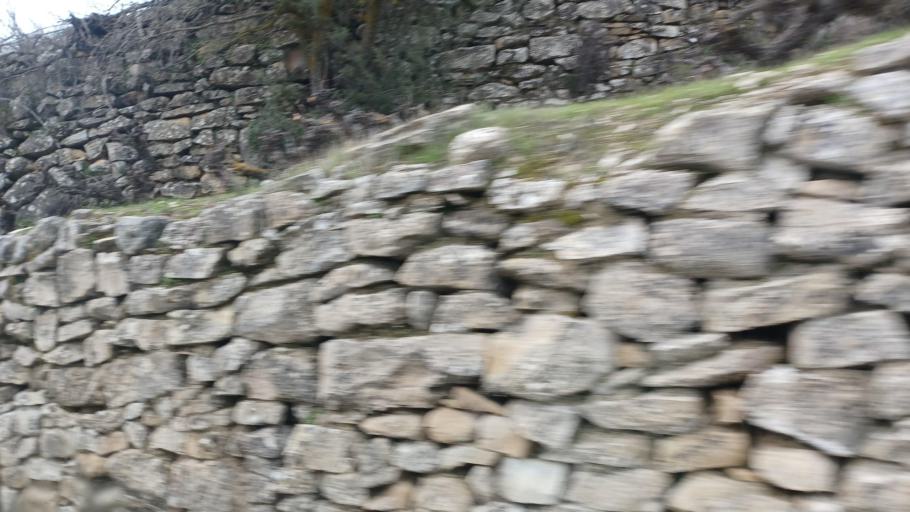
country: CY
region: Limassol
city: Pachna
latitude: 34.7734
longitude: 32.7660
